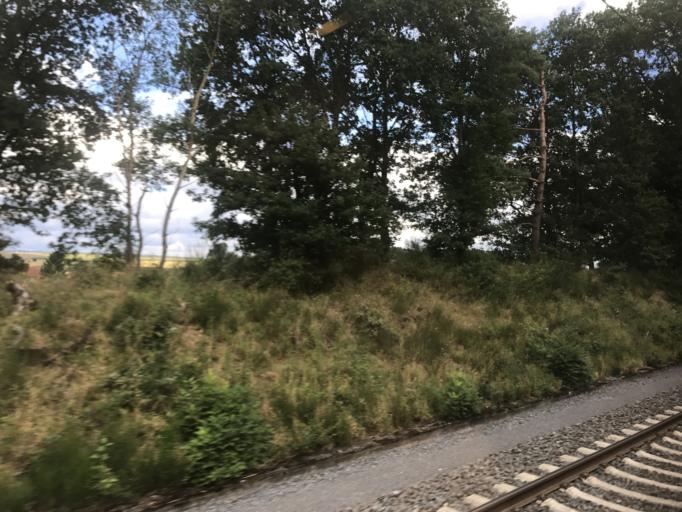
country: DE
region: Hesse
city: Neustadt (Hessen)
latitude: 50.8599
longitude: 9.1251
